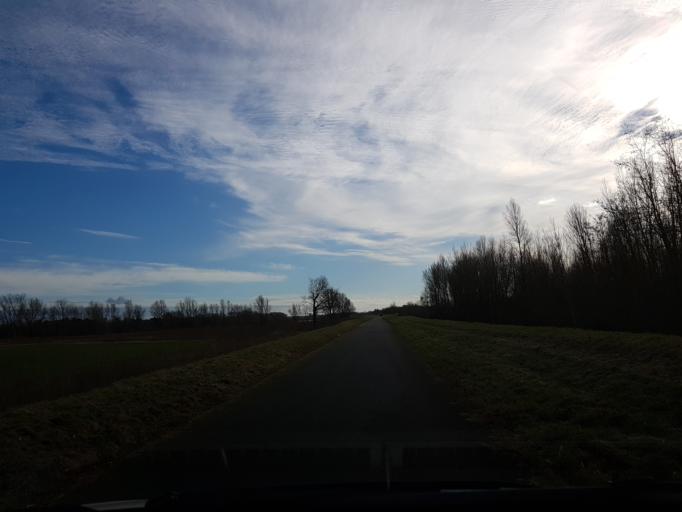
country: FR
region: Centre
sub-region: Departement du Loiret
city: Checy
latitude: 47.8713
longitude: 2.0256
